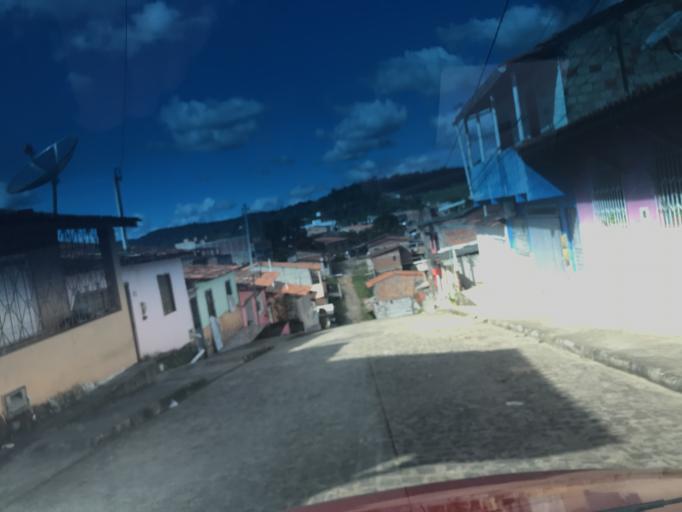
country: BR
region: Bahia
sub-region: Gandu
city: Gandu
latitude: -13.7468
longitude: -39.4929
